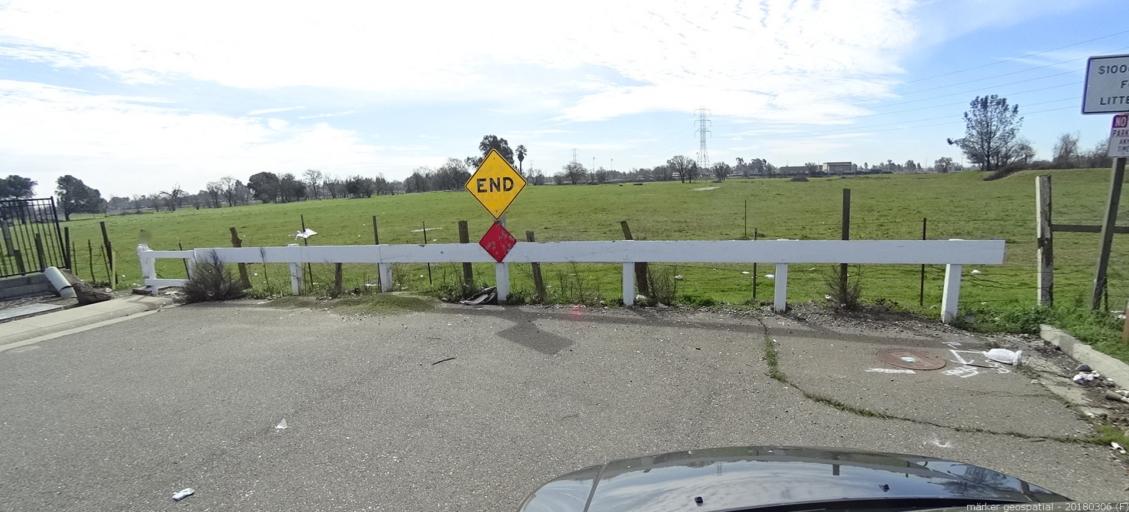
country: US
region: California
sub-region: Sacramento County
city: Vineyard
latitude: 38.4599
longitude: -121.3407
